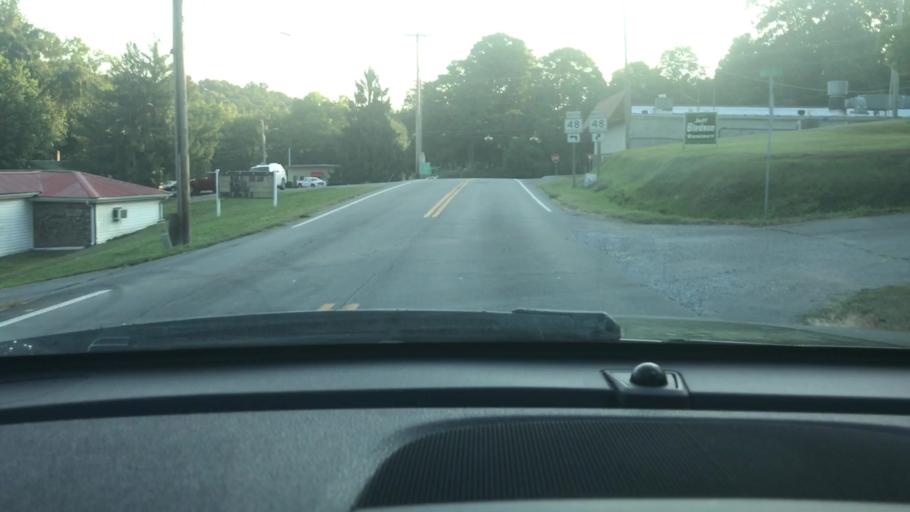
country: US
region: Tennessee
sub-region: Dickson County
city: Charlotte
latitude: 36.1770
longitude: -87.3408
